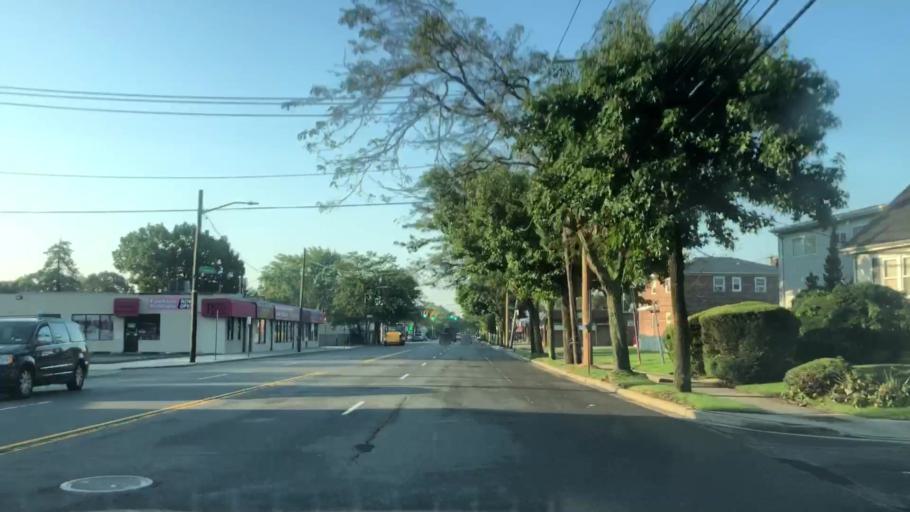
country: US
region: New York
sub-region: Nassau County
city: North Massapequa
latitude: 40.7034
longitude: -73.4619
